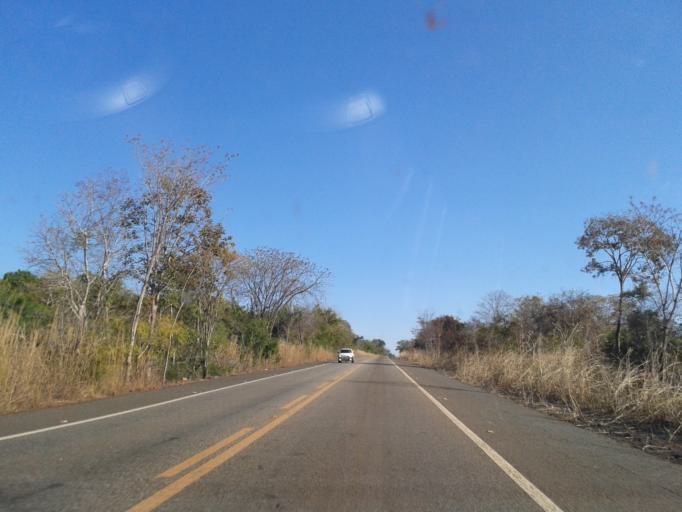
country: BR
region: Goias
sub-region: Mozarlandia
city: Mozarlandia
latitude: -15.0399
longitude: -50.6047
